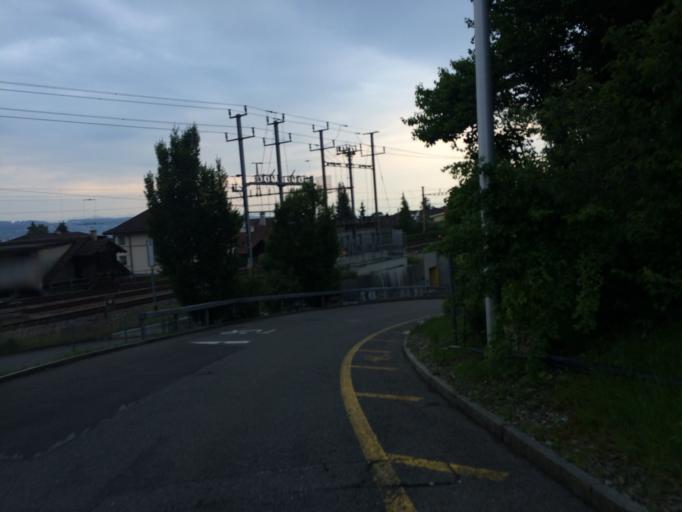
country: CH
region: Zurich
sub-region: Bezirk Horgen
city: Horgen / Oberdorf
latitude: 47.2578
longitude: 8.5902
